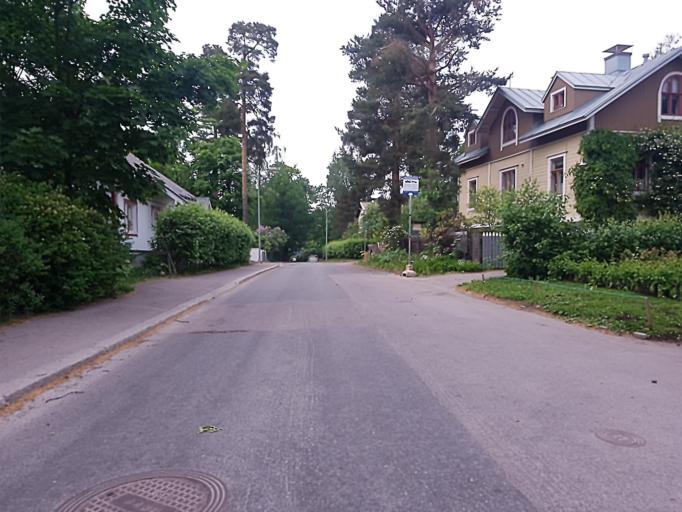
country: FI
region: Uusimaa
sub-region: Helsinki
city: Helsinki
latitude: 60.2253
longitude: 24.9713
